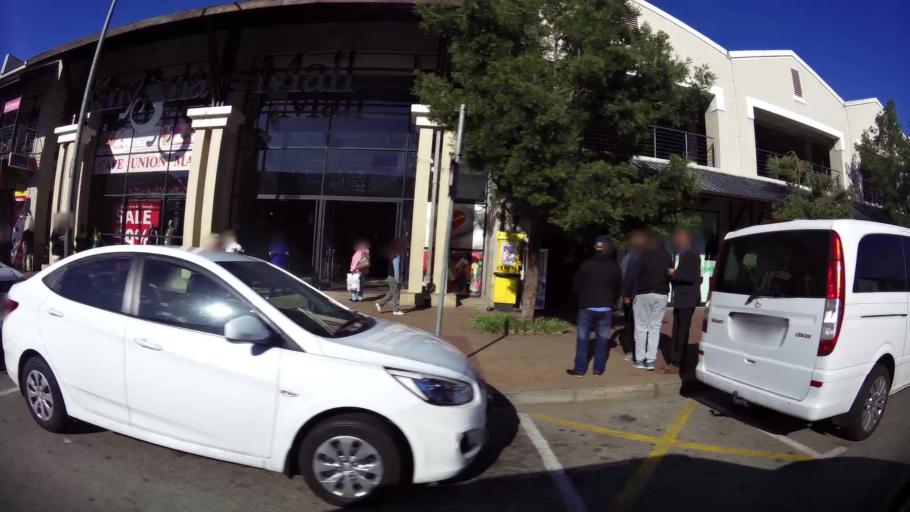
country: ZA
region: Western Cape
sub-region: Eden District Municipality
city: Knysna
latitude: -34.0350
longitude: 23.0460
